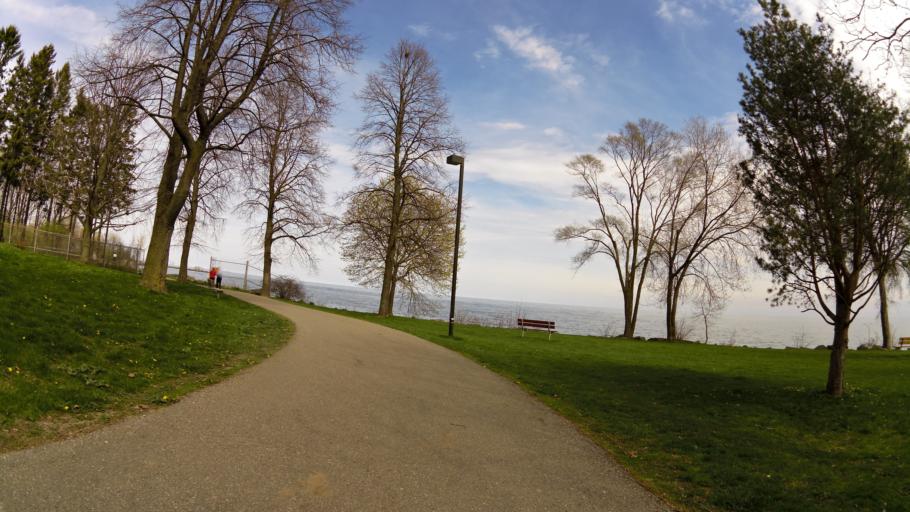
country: CA
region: Ontario
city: Mississauga
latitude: 43.5410
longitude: -79.5887
